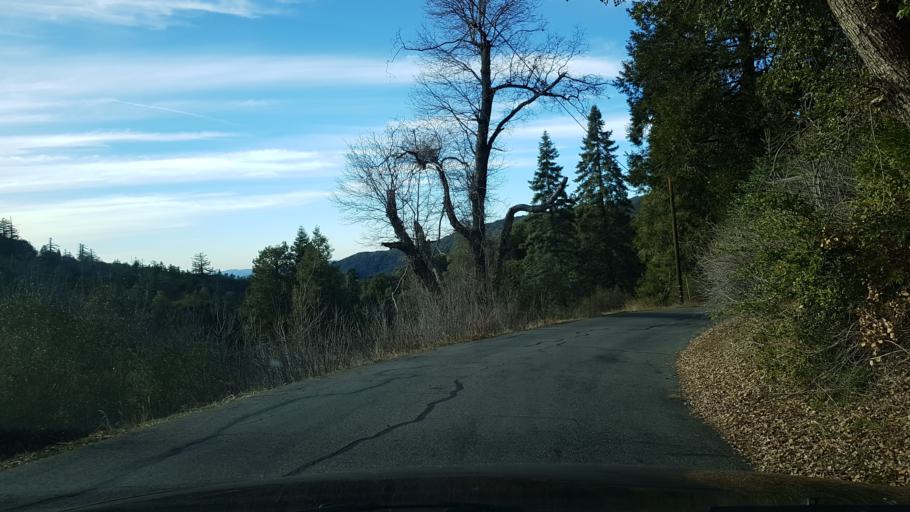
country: US
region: California
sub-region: Riverside County
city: Aguanga
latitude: 33.3383
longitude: -116.9097
